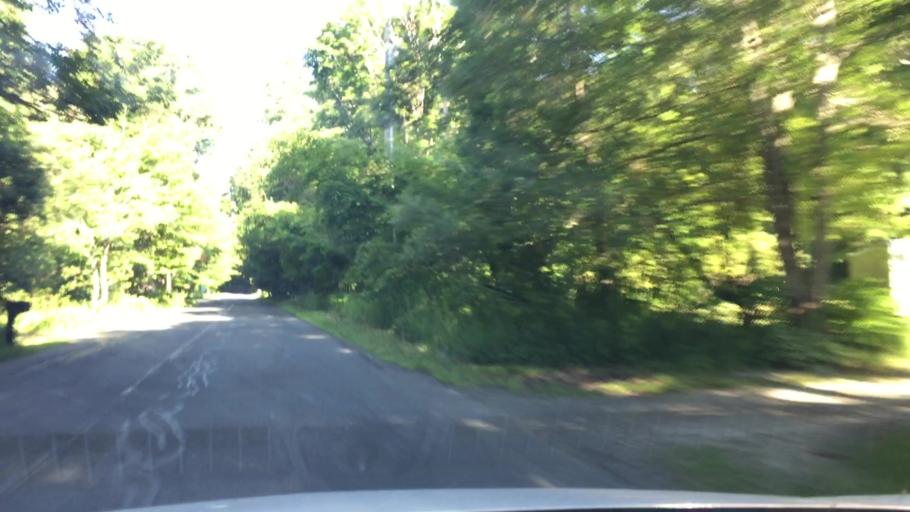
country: US
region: Massachusetts
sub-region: Berkshire County
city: Becket
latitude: 42.3173
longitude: -73.1095
